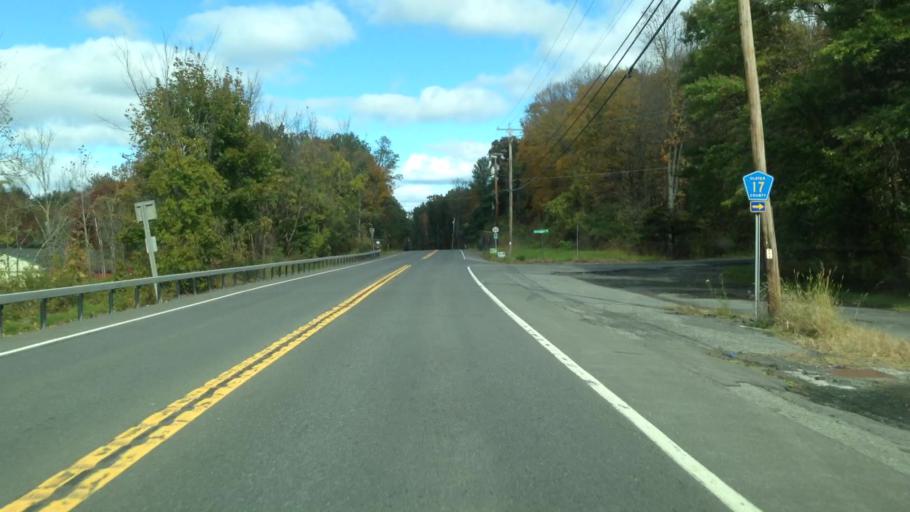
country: US
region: New York
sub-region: Ulster County
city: New Paltz
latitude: 41.7821
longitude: -74.0719
